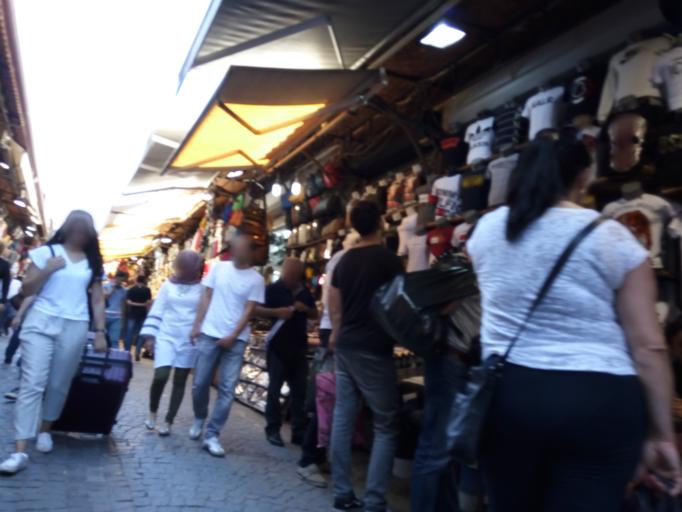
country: TR
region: Istanbul
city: Eminoenue
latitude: 41.0105
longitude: 28.9663
